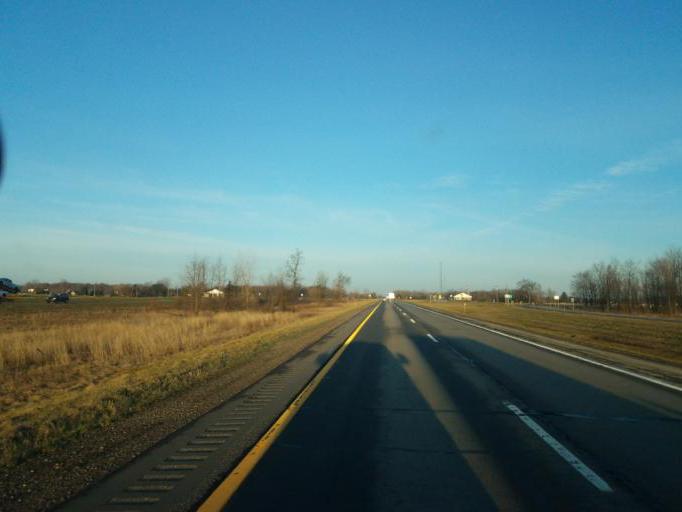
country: US
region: Michigan
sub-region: Ingham County
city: Webberville
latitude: 42.6512
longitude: -84.1250
